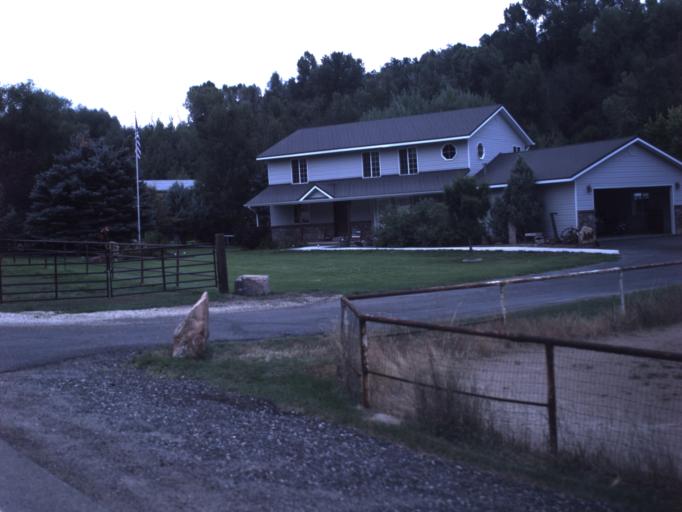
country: US
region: Utah
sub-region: Summit County
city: Oakley
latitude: 40.7259
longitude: -111.3315
